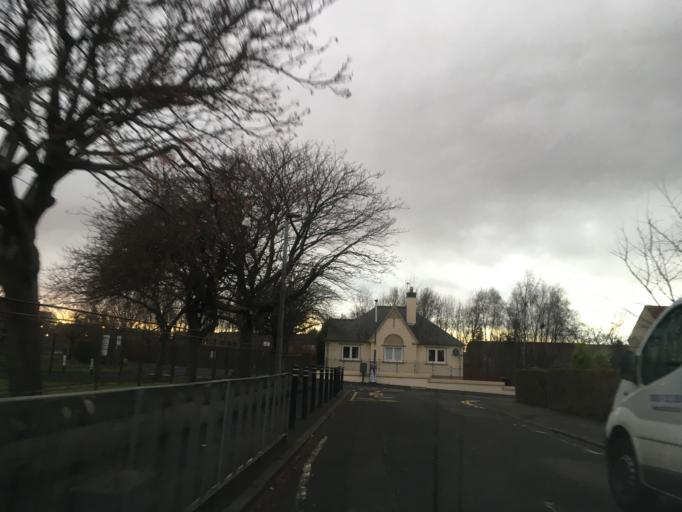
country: GB
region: Scotland
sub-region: Edinburgh
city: Colinton
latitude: 55.9214
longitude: -3.2613
